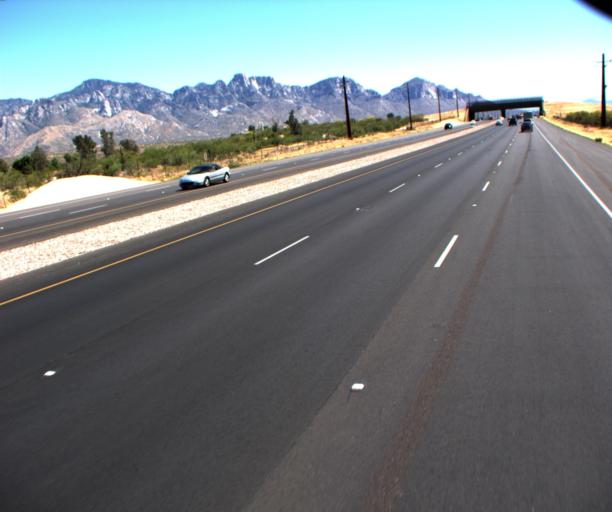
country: US
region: Arizona
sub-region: Pima County
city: Catalina
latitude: 32.4730
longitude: -110.9237
